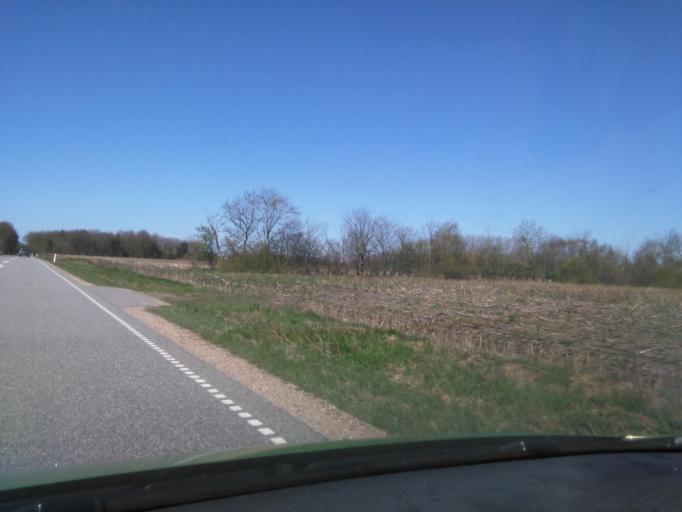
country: DK
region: South Denmark
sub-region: Billund Kommune
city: Grindsted
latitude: 55.6993
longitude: 8.7972
